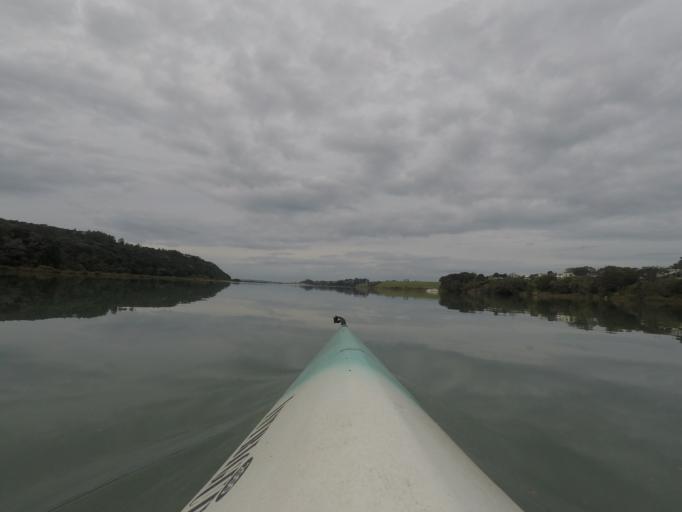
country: NZ
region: Auckland
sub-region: Auckland
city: Rothesay Bay
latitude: -36.6727
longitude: 174.7168
